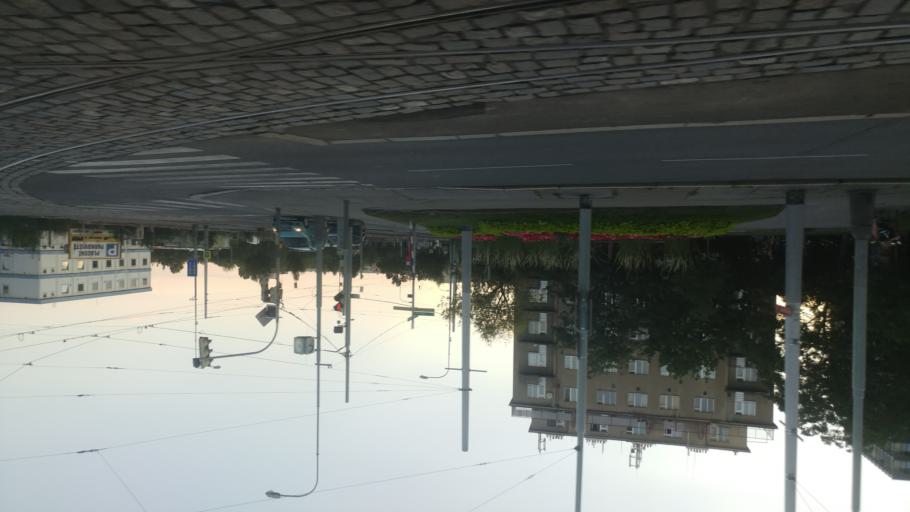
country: CZ
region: Praha
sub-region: Praha 8
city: Liben
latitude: 50.0843
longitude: 14.4704
